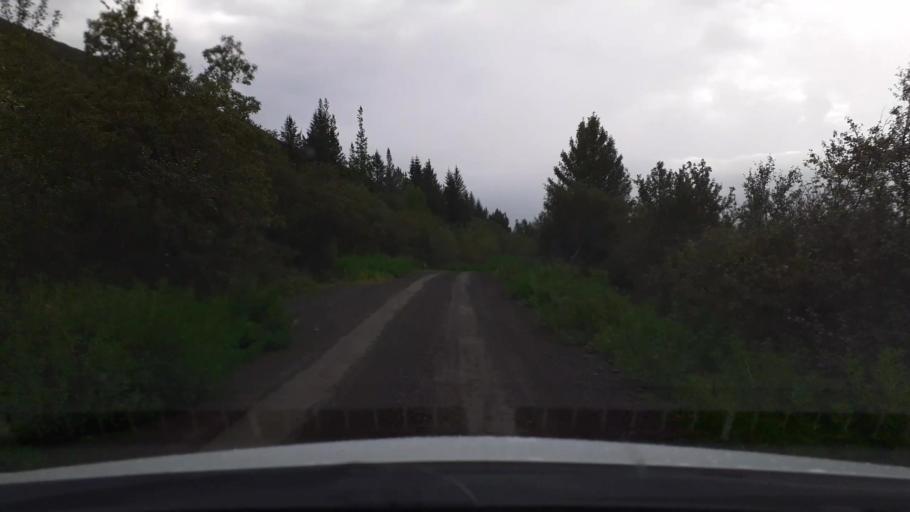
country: IS
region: Capital Region
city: Mosfellsbaer
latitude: 64.4938
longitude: -21.3479
